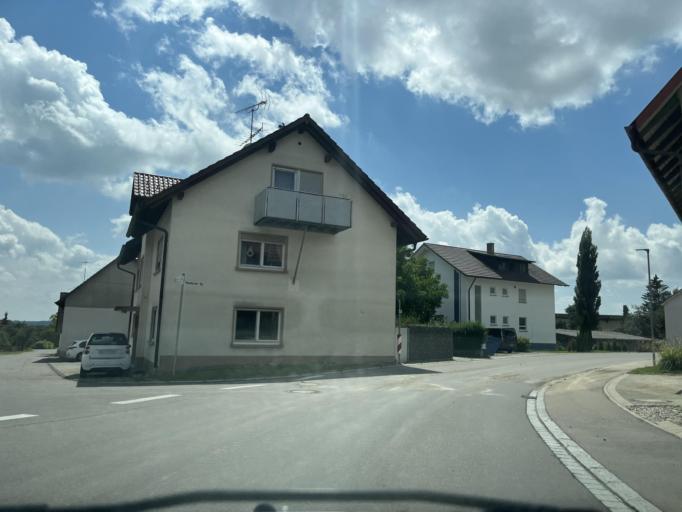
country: DE
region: Baden-Wuerttemberg
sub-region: Tuebingen Region
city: Messkirch
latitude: 48.0149
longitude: 9.0982
